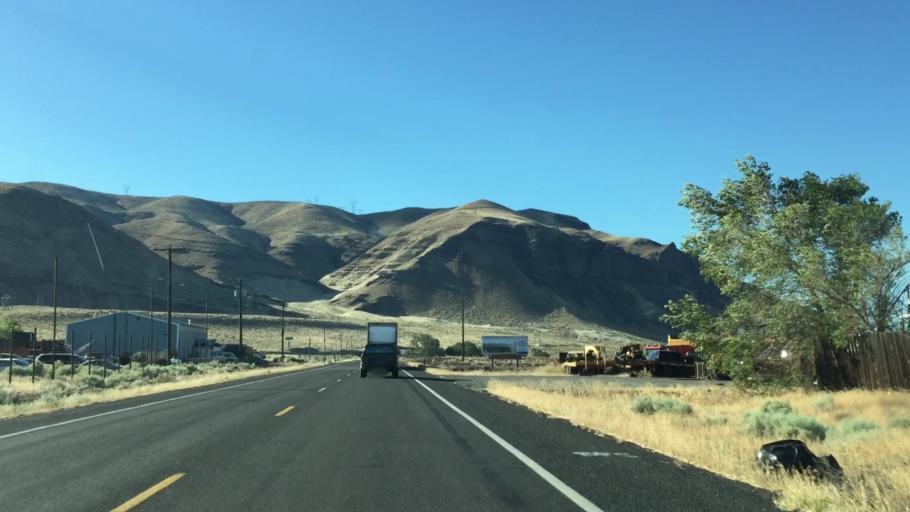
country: US
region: Washington
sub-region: Grant County
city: Mattawa
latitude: 46.8217
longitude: -119.9260
